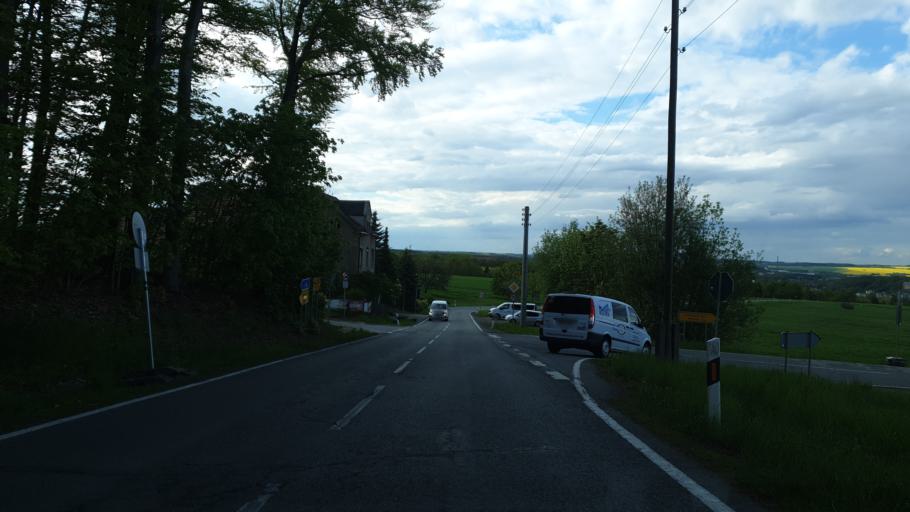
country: DE
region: Saxony
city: Lichtenstein
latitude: 50.7352
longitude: 12.6351
